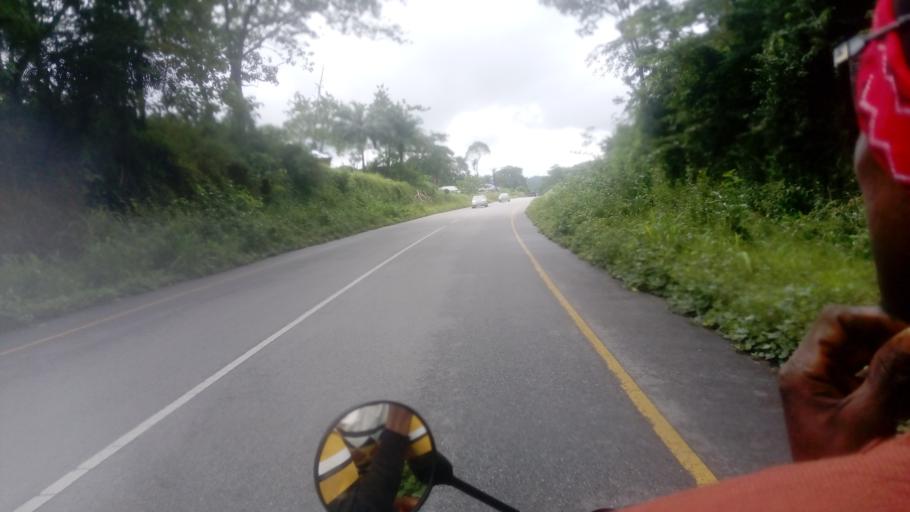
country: SL
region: Northern Province
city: Makali
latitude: 8.6332
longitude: -11.6694
